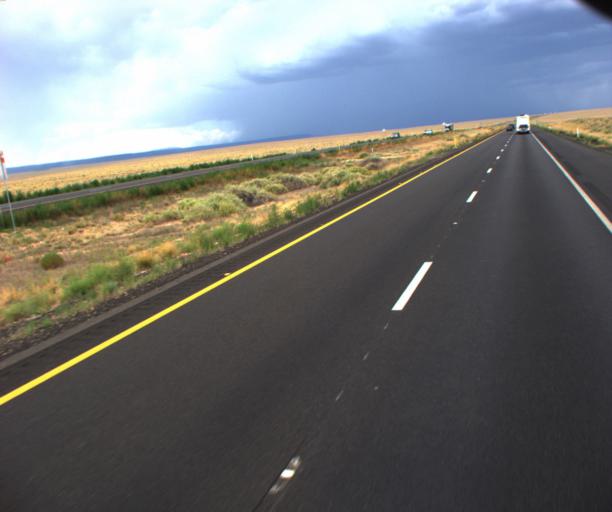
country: US
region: Arizona
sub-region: Coconino County
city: LeChee
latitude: 35.1183
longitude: -111.1290
